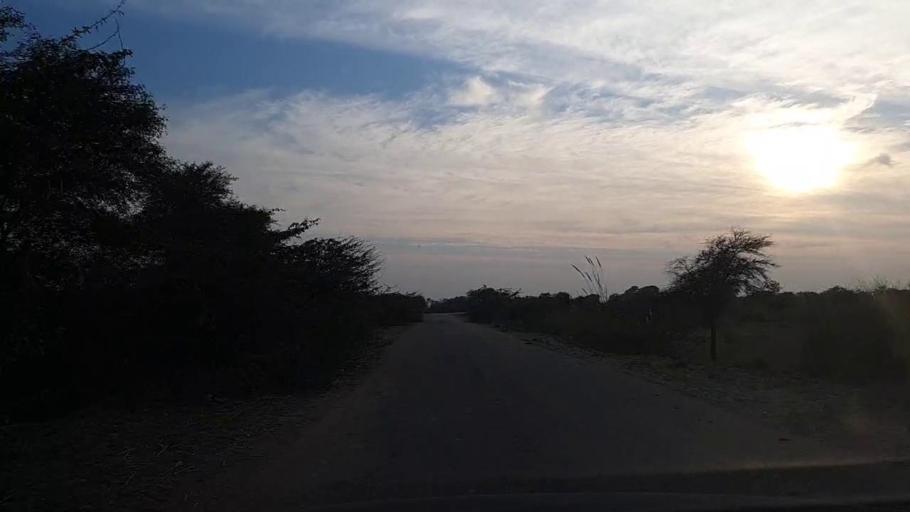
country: PK
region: Sindh
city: Nawabshah
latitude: 26.4004
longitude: 68.4808
